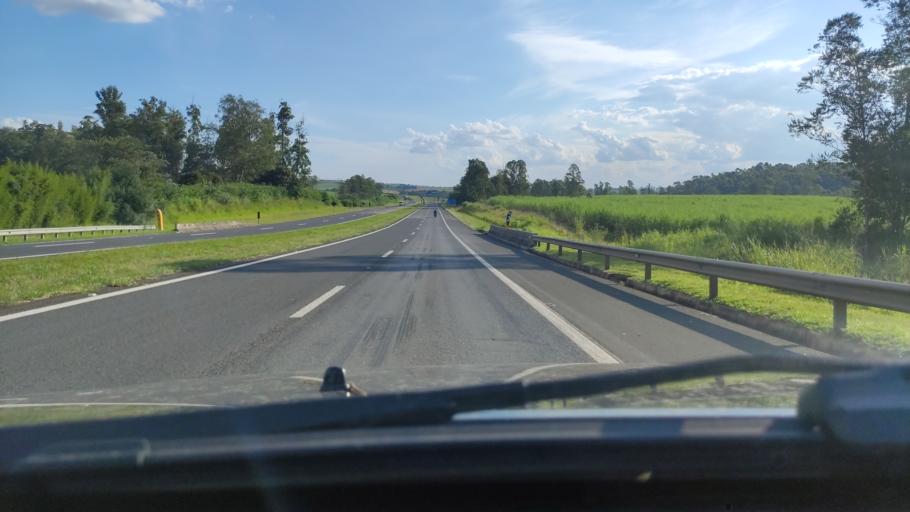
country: BR
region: Sao Paulo
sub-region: Itapira
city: Itapira
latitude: -22.4506
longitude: -46.8896
